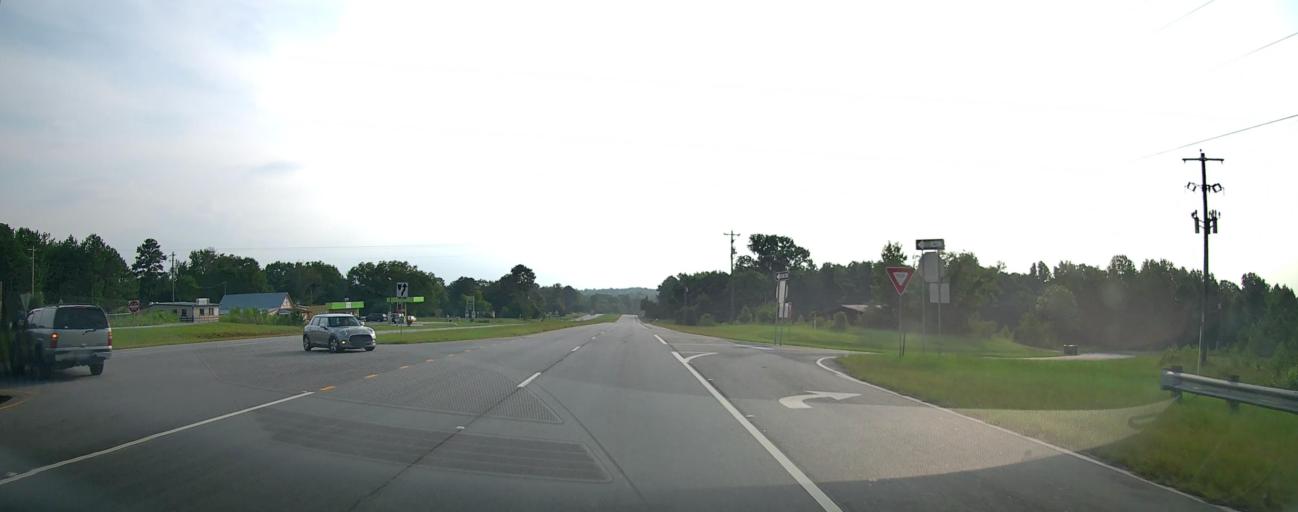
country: US
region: Georgia
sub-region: Talbot County
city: Talbotton
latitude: 32.5541
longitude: -84.6631
